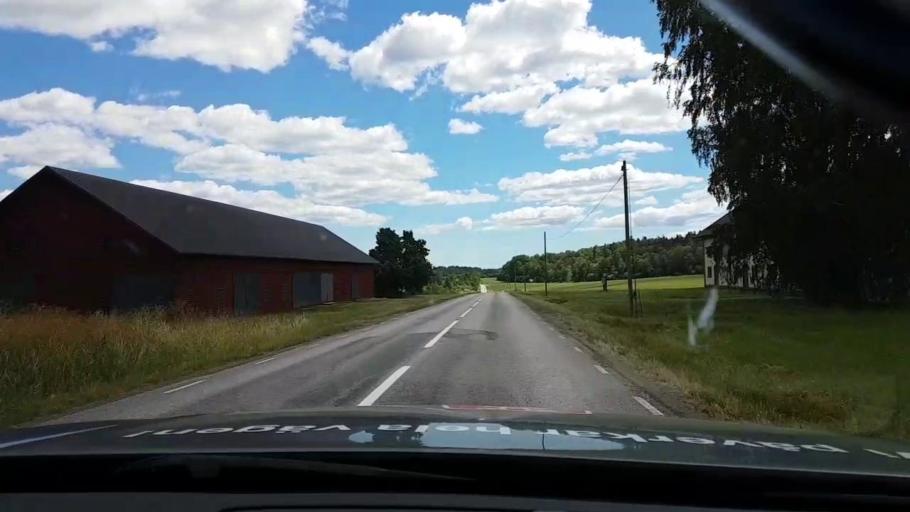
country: SE
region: Kalmar
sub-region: Vasterviks Kommun
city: Forserum
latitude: 58.0472
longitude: 16.4121
